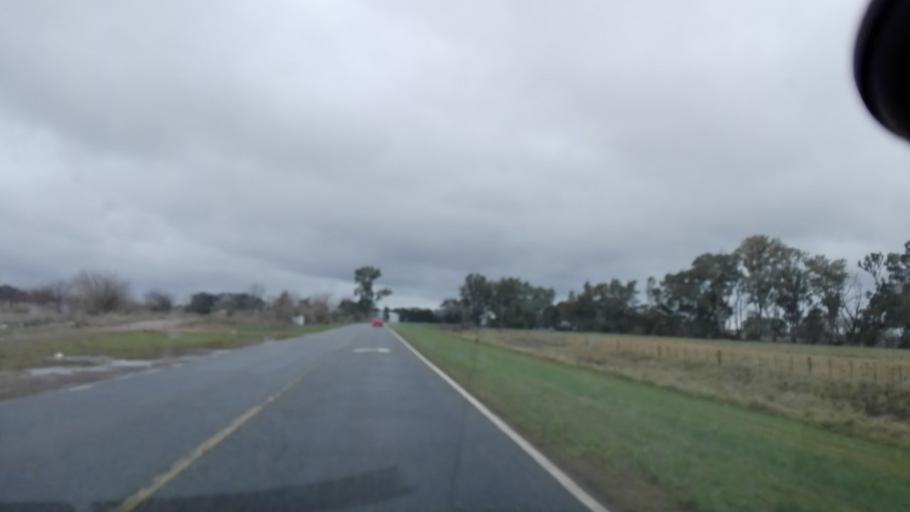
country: AR
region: Buenos Aires
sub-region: Partido de Brandsen
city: Brandsen
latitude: -35.1773
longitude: -58.2800
